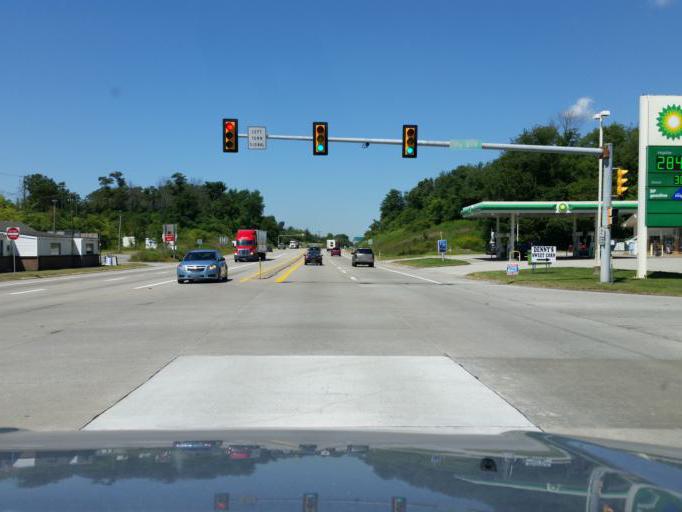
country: US
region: Pennsylvania
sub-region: Westmoreland County
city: Delmont
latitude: 40.4030
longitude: -79.5226
